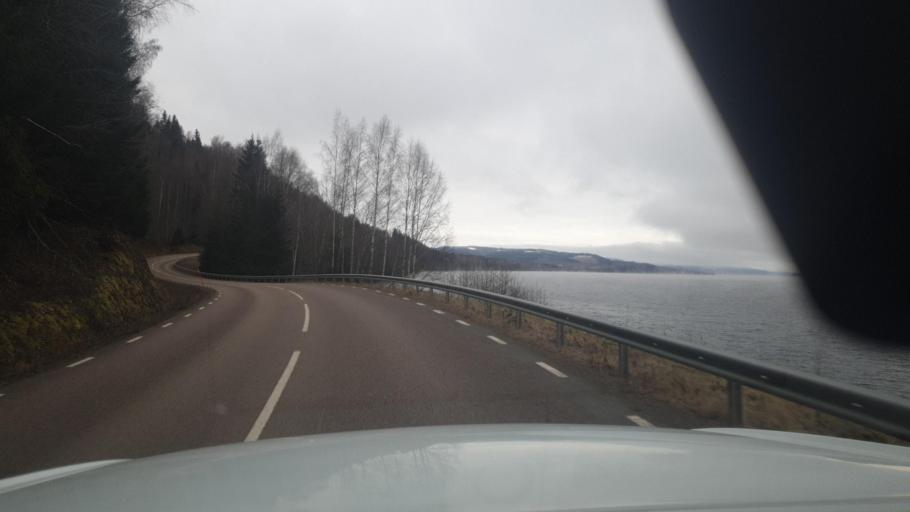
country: SE
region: Vaermland
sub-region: Sunne Kommun
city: Sunne
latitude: 59.8219
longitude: 13.0005
